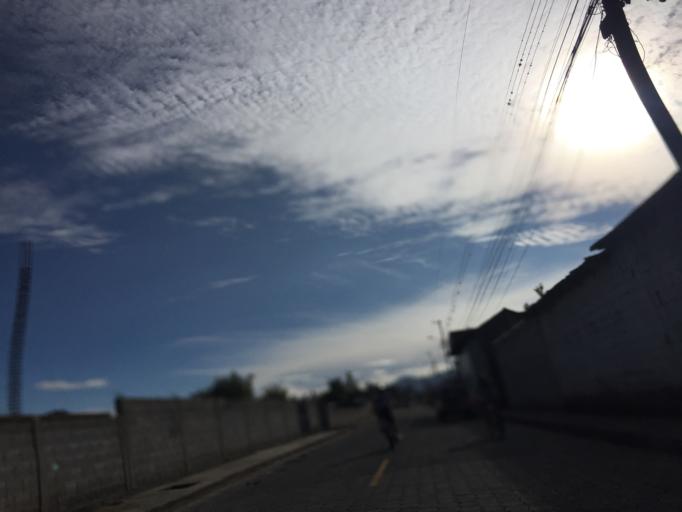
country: EC
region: Imbabura
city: Atuntaqui
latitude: 0.3390
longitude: -78.1906
